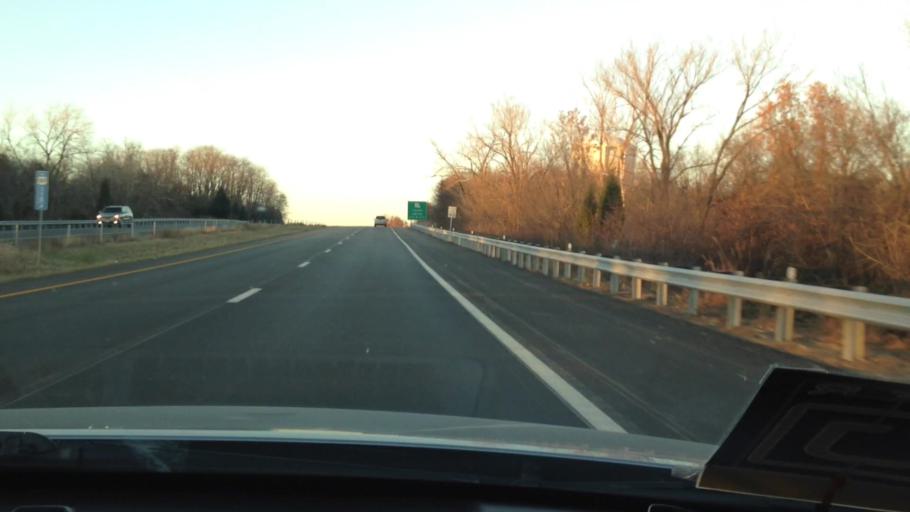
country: US
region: Missouri
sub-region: Clay County
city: Gladstone
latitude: 39.2266
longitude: -94.5890
